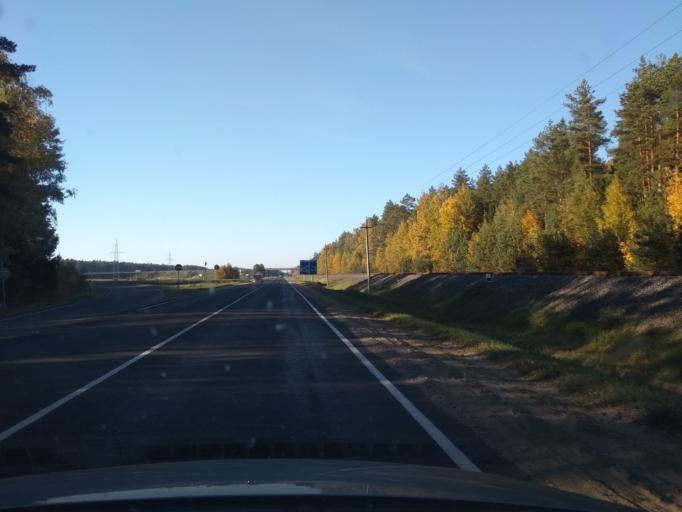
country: BY
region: Brest
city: Nyakhachava
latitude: 52.5716
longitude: 25.1170
